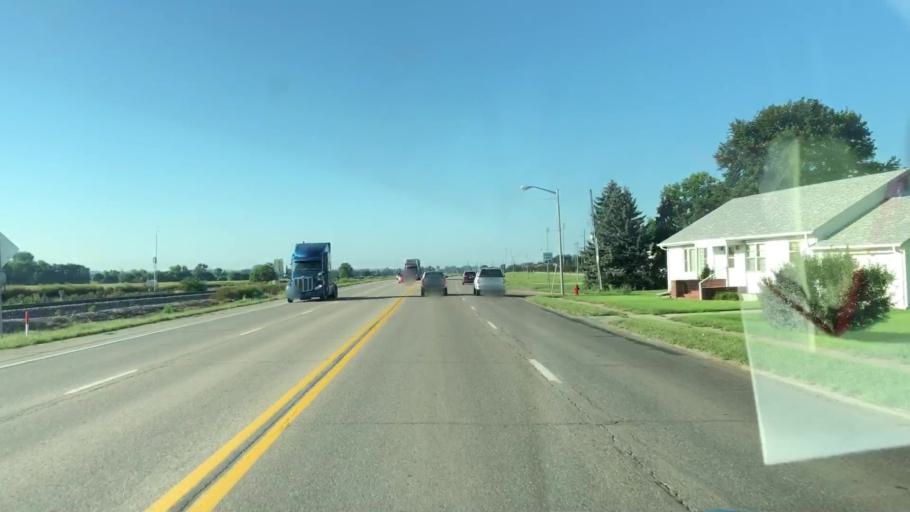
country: US
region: Iowa
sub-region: Woodbury County
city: Sioux City
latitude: 42.6250
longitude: -96.2925
